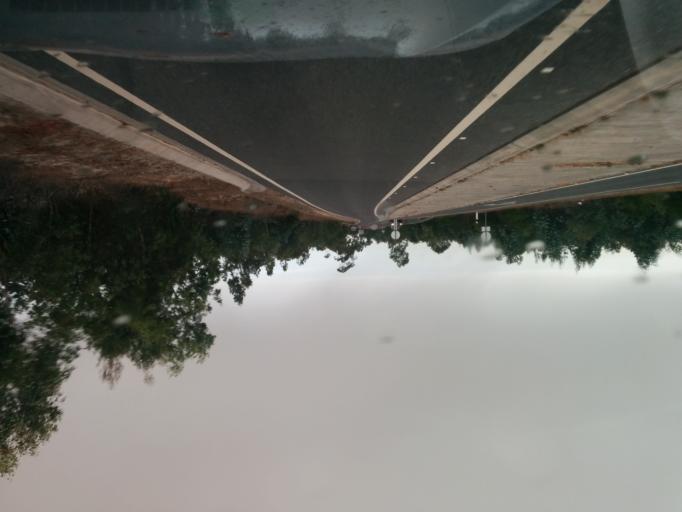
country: PT
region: Beja
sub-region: Odemira
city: Vila Nova de Milfontes
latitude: 37.6363
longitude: -8.7538
